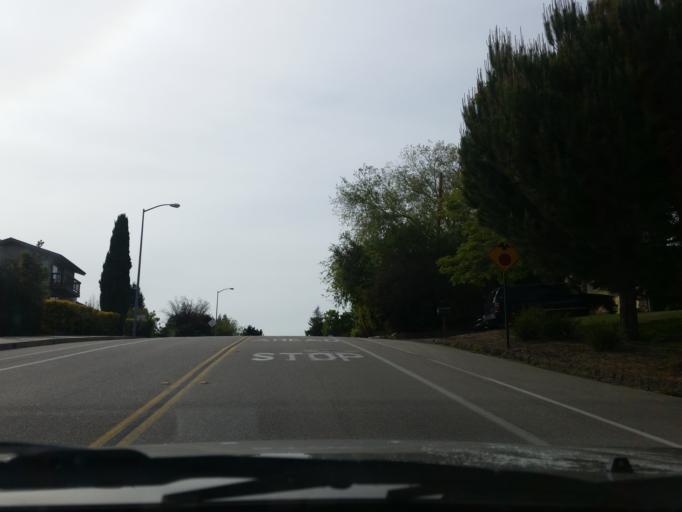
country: US
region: California
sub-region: San Luis Obispo County
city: Arroyo Grande
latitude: 35.1306
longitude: -120.5750
